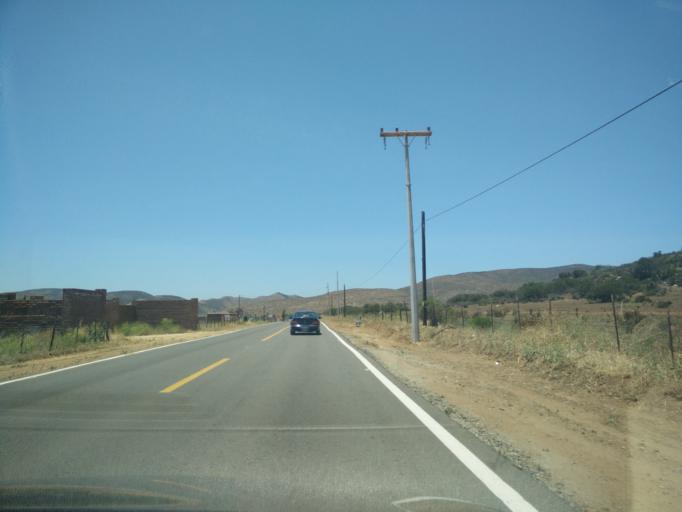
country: MX
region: Baja California
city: El Sauzal
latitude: 32.0058
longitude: -116.6764
